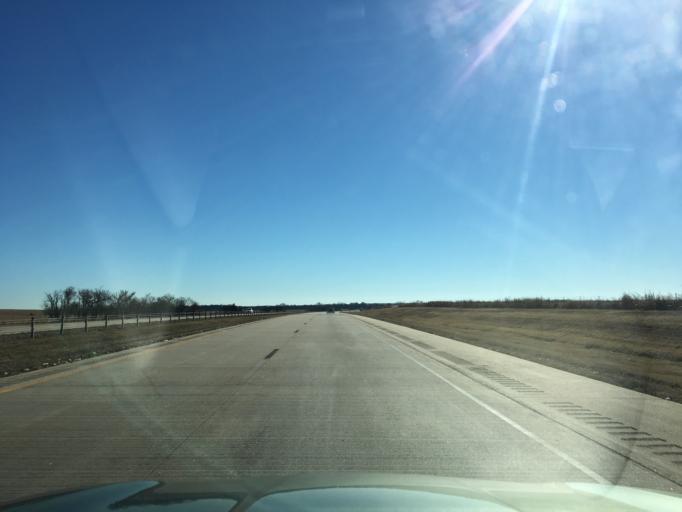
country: US
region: Oklahoma
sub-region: Kay County
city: Tonkawa
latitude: 36.4923
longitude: -97.3305
